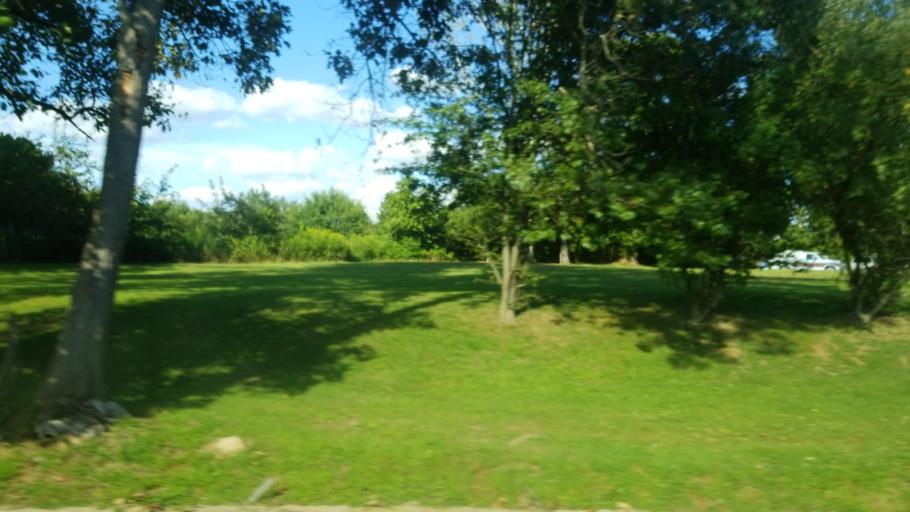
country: US
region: Illinois
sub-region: Saline County
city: Harrisburg
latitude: 37.8281
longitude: -88.5496
